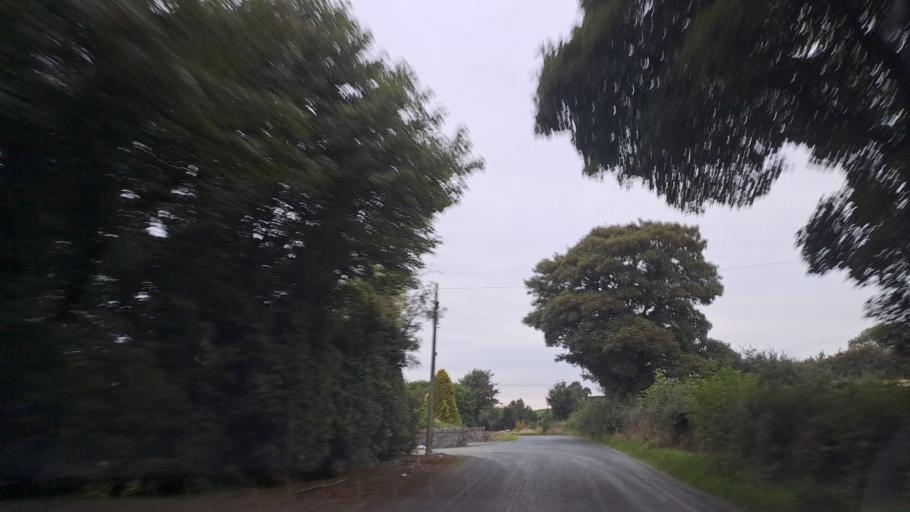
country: IE
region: Ulster
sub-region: County Monaghan
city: Carrickmacross
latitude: 54.0264
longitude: -6.7946
